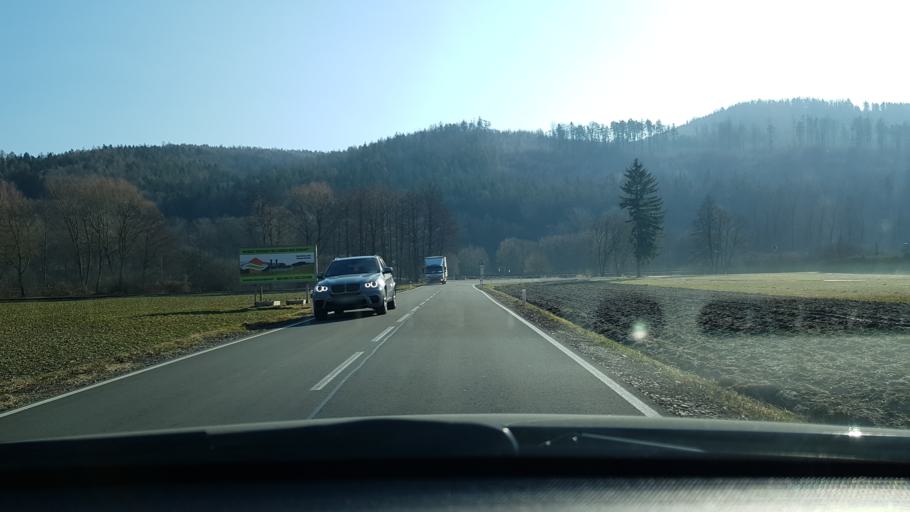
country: CZ
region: Olomoucky
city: Dolni Bohdikov
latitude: 49.9988
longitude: 16.8924
